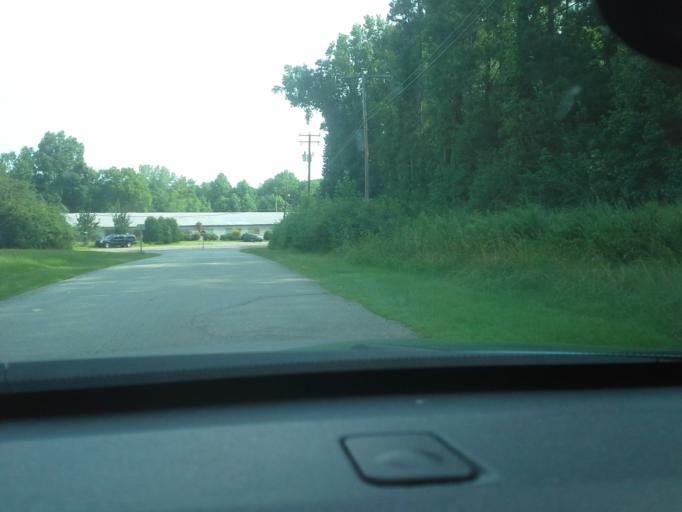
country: US
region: North Carolina
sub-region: Washington County
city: Plymouth
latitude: 35.8624
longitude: -76.7583
